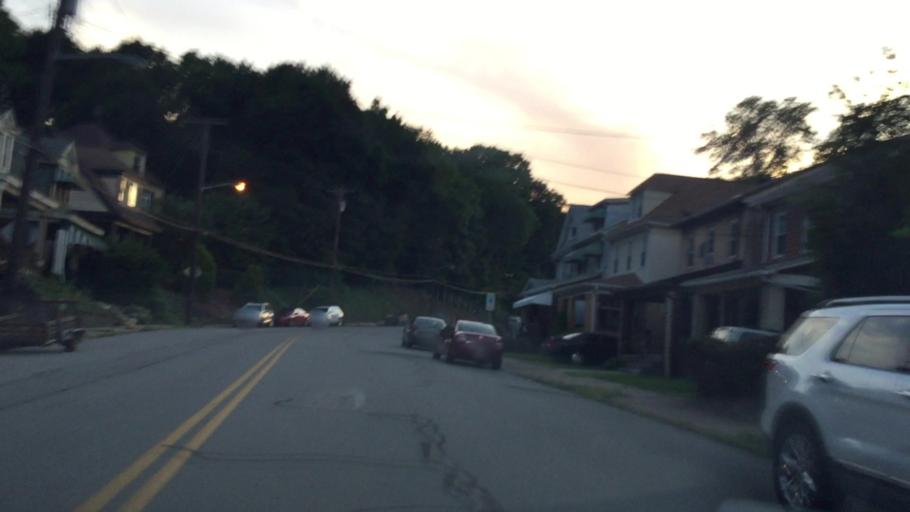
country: US
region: Pennsylvania
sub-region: Allegheny County
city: Millvale
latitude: 40.4880
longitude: -80.0143
